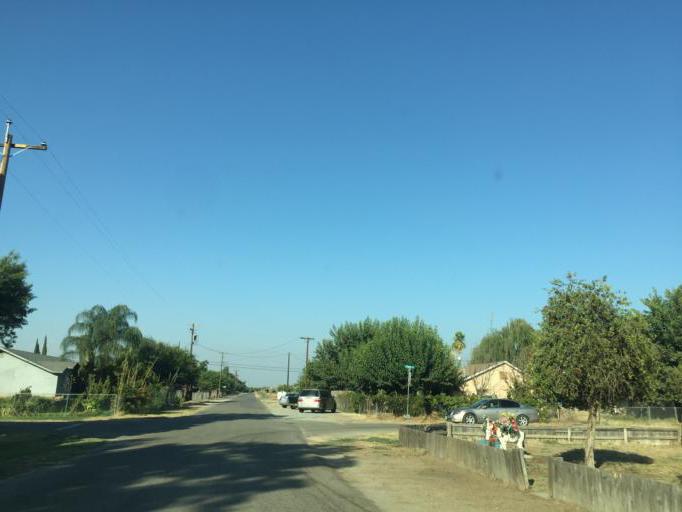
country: US
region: California
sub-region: Tulare County
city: London
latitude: 36.4528
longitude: -119.4859
